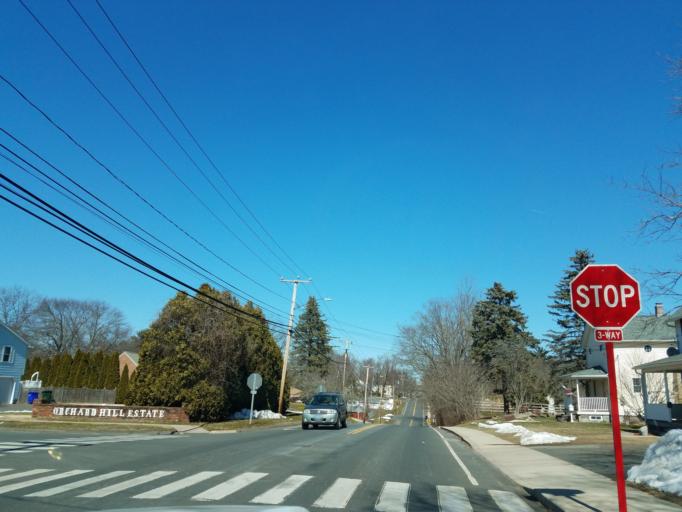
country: US
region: Connecticut
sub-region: Hartford County
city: Windsor Locks
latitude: 41.9228
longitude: -72.6334
